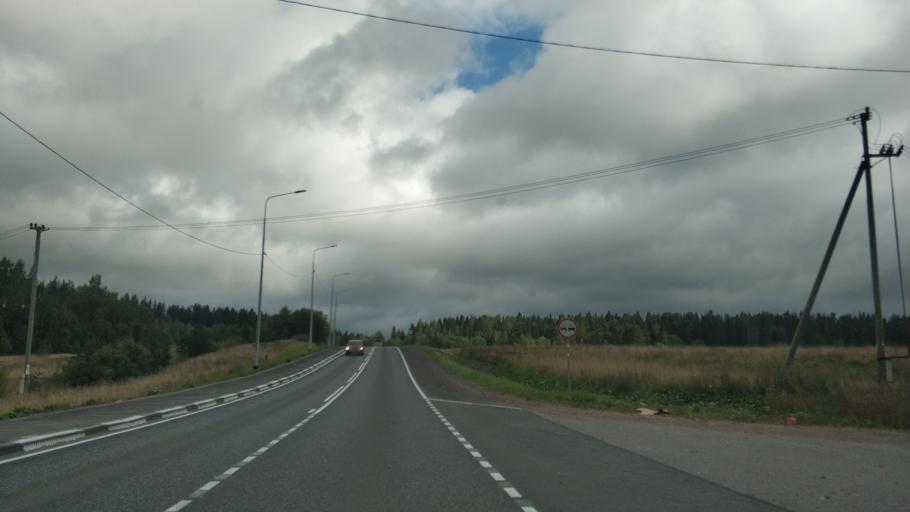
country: RU
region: Republic of Karelia
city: Khelyulya
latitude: 61.7622
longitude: 30.6565
